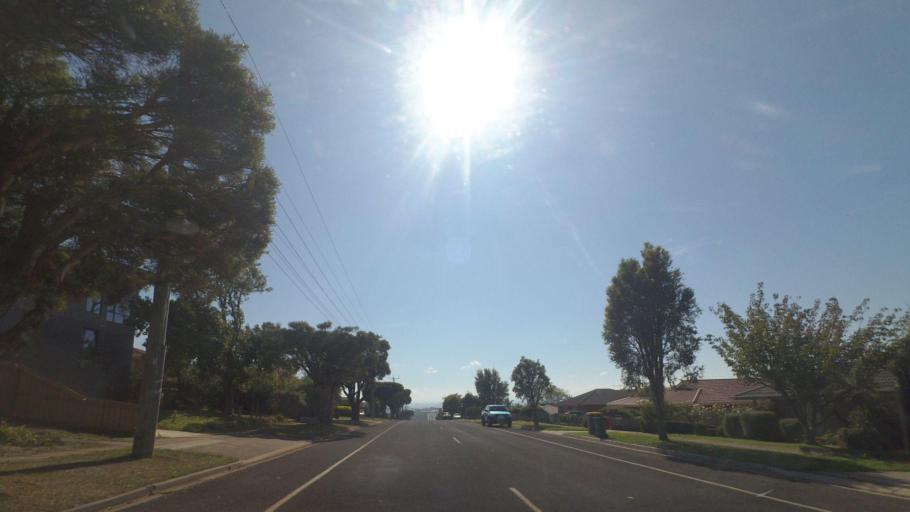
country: AU
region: Victoria
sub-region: Baw Baw
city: Warragul
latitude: -38.1590
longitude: 145.9495
